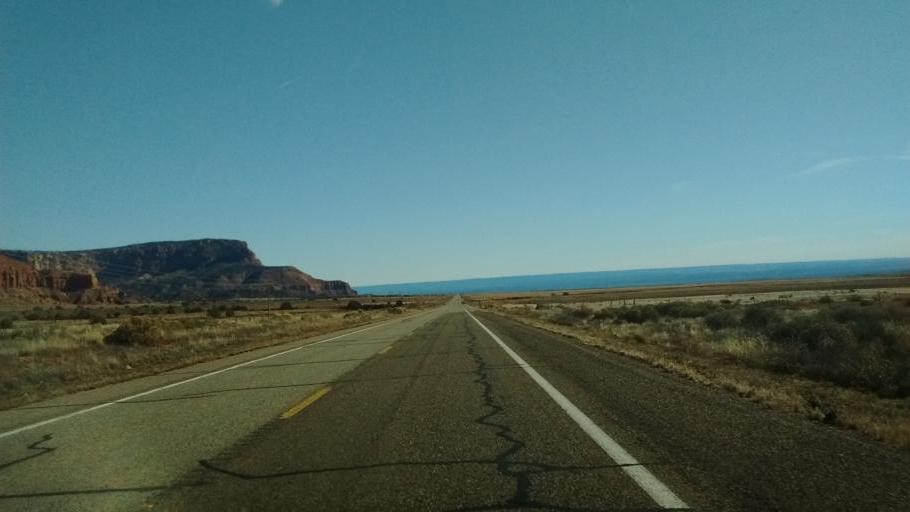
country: US
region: Arizona
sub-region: Mohave County
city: Colorado City
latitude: 36.8778
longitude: -112.8826
